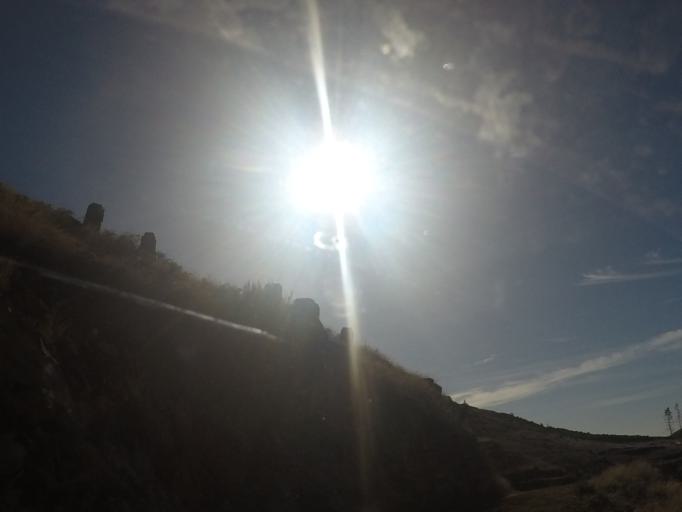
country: PT
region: Madeira
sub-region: Funchal
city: Nossa Senhora do Monte
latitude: 32.7082
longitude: -16.9008
